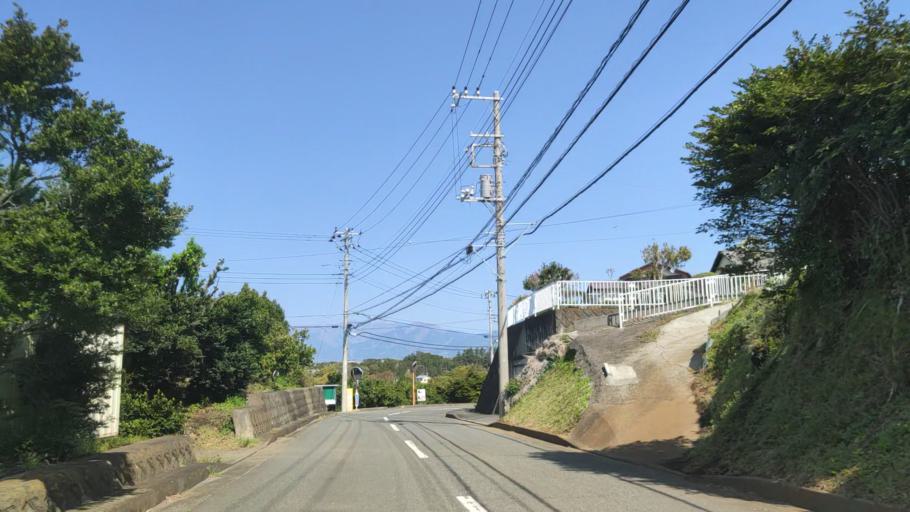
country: JP
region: Kanagawa
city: Ninomiya
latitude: 35.3234
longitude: 139.2582
